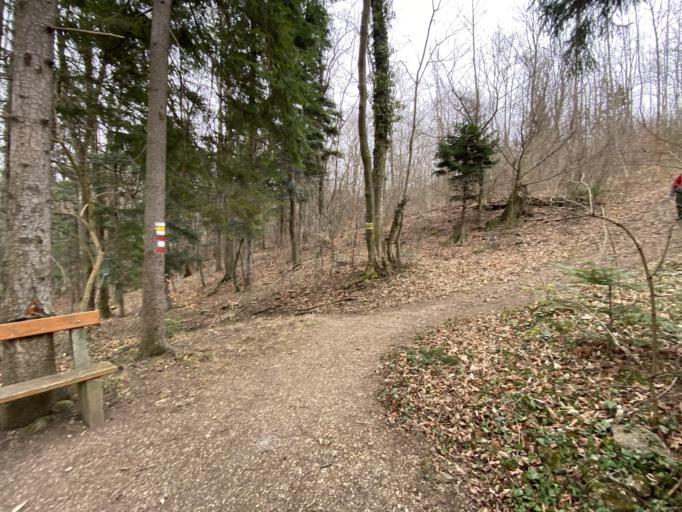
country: AT
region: Lower Austria
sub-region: Politischer Bezirk Modling
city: Gaaden
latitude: 48.0246
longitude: 16.1993
